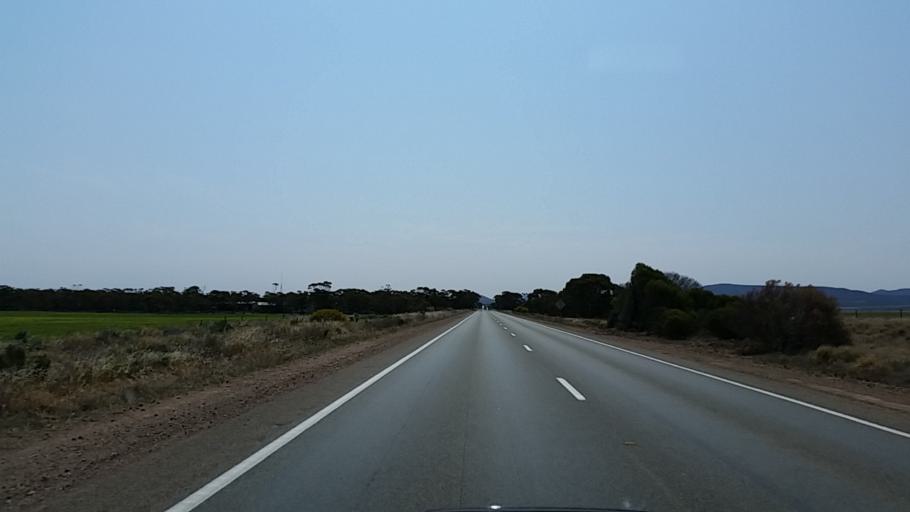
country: AU
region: South Australia
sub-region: Port Pirie City and Dists
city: Port Pirie
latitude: -32.9227
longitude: 137.9824
